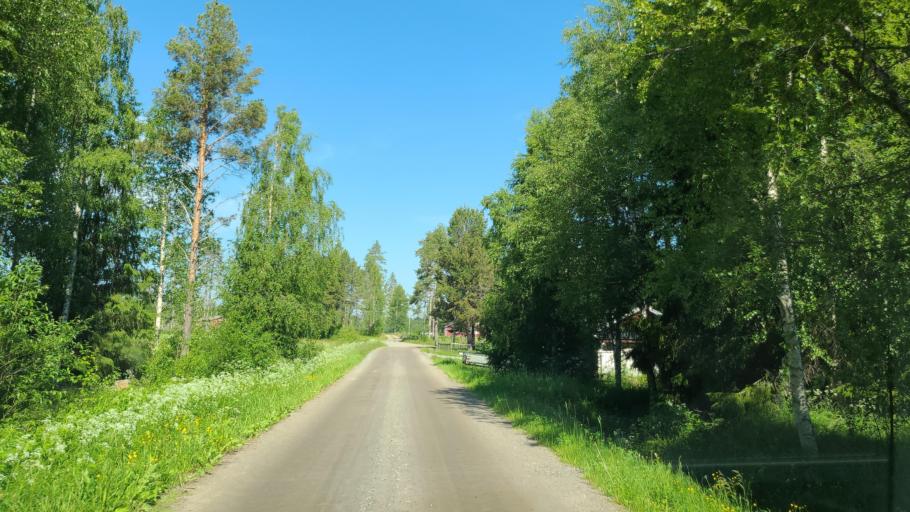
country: SE
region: Vaesterbotten
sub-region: Robertsfors Kommun
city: Robertsfors
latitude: 64.0860
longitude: 20.8420
